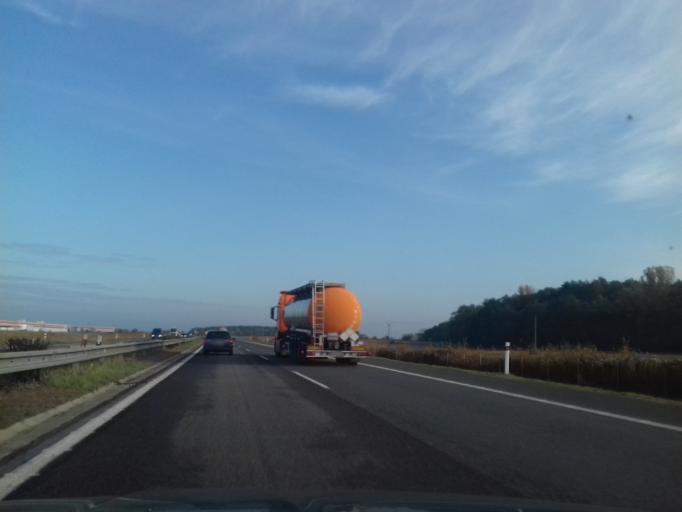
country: SK
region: Bratislavsky
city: Stupava
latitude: 48.3112
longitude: 17.0192
